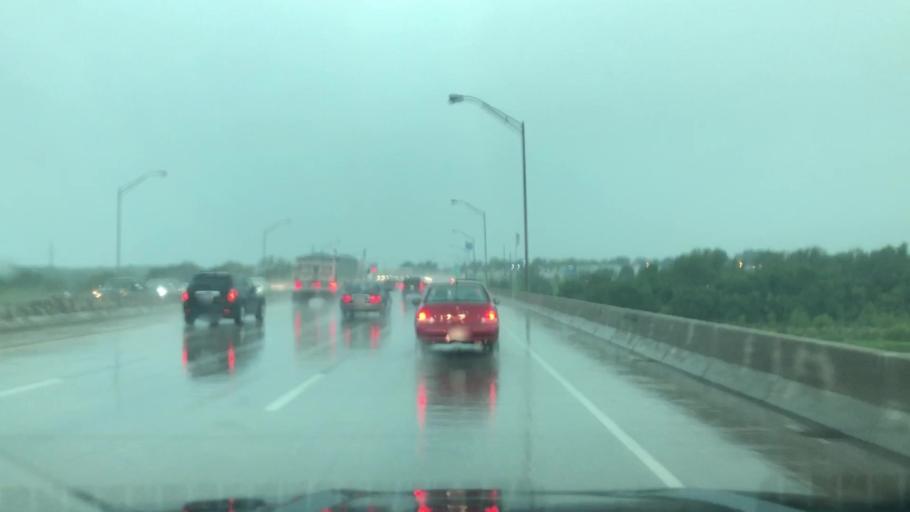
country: US
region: Oklahoma
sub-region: Tulsa County
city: Tulsa
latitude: 36.0900
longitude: -95.9888
